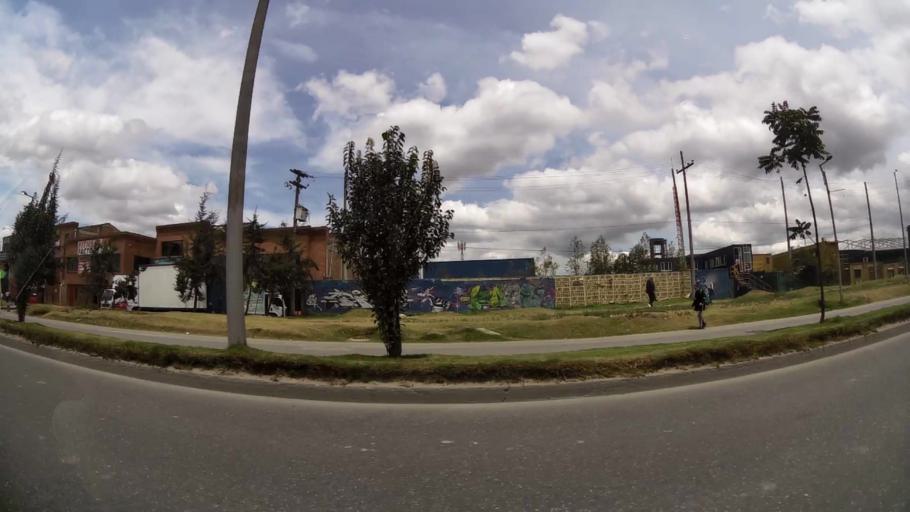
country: CO
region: Bogota D.C.
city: Bogota
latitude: 4.6549
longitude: -74.1412
